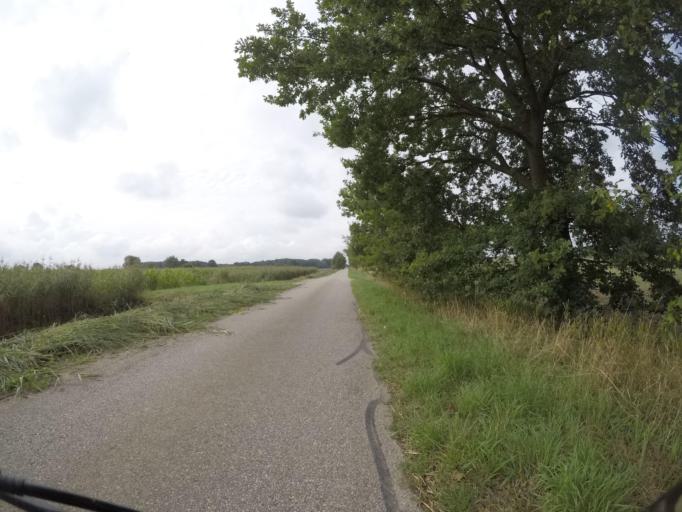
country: DE
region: Lower Saxony
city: Neu Darchau
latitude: 53.3012
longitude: 10.8821
